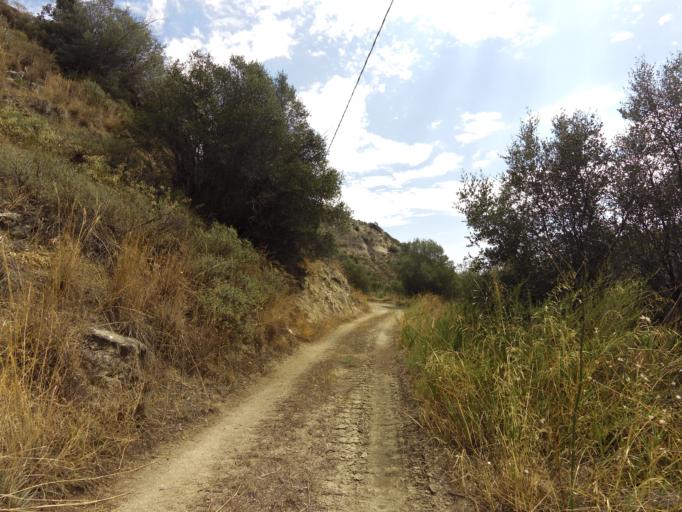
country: IT
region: Calabria
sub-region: Provincia di Reggio Calabria
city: Camini
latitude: 38.4526
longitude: 16.4733
